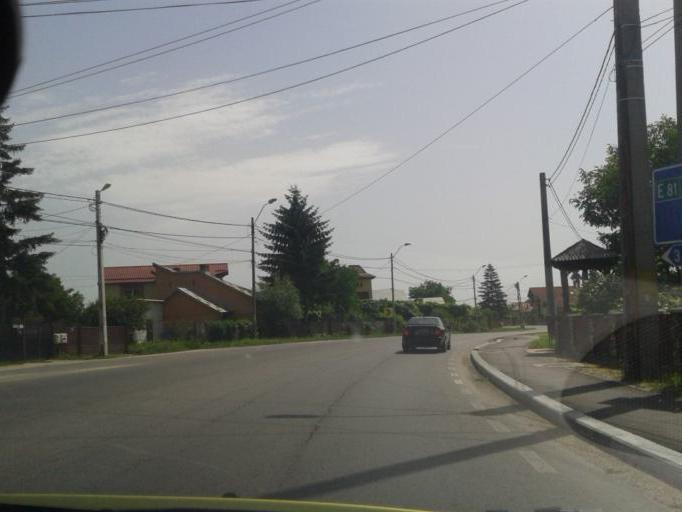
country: RO
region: Arges
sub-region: Comuna Bascov
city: Bascov
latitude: 44.8886
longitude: 24.8143
